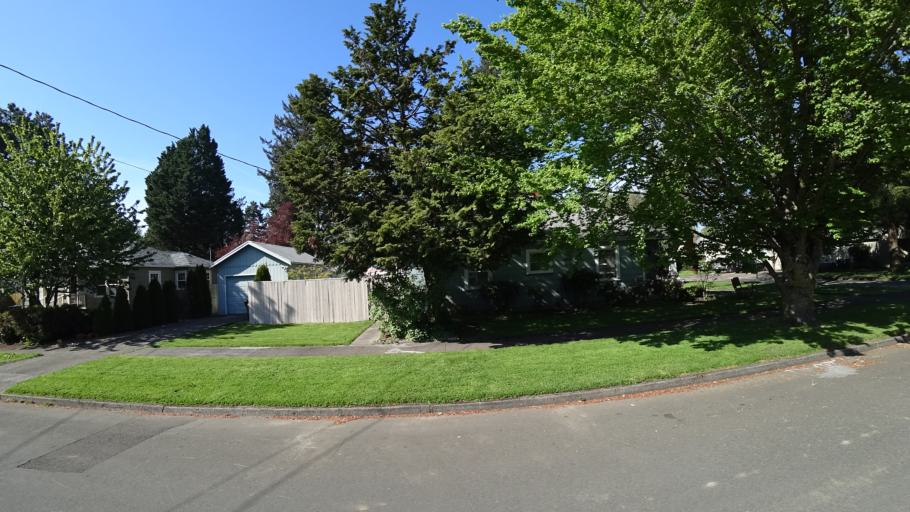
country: US
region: Oregon
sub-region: Washington County
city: Hillsboro
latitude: 45.5273
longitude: -122.9882
